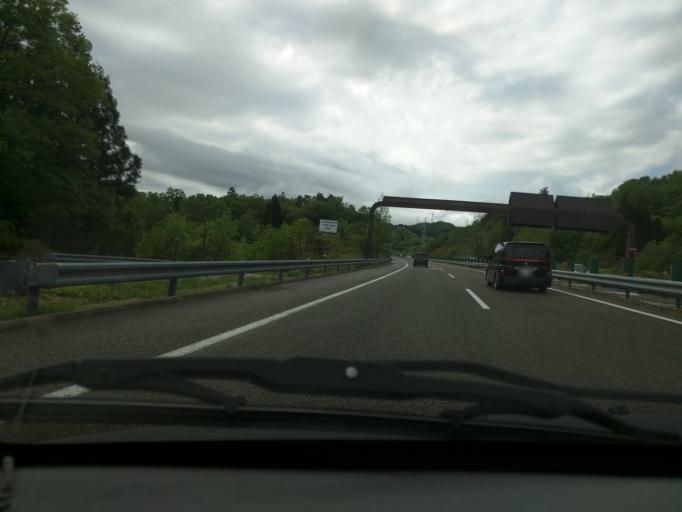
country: JP
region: Niigata
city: Joetsu
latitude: 37.1362
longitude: 138.2137
